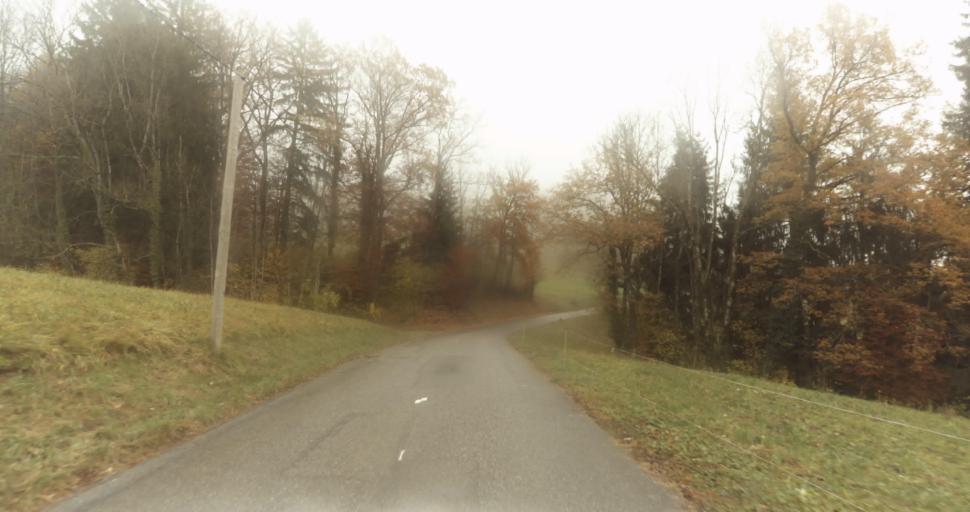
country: FR
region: Rhone-Alpes
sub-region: Departement de la Haute-Savoie
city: Villaz
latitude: 45.9756
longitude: 6.1875
